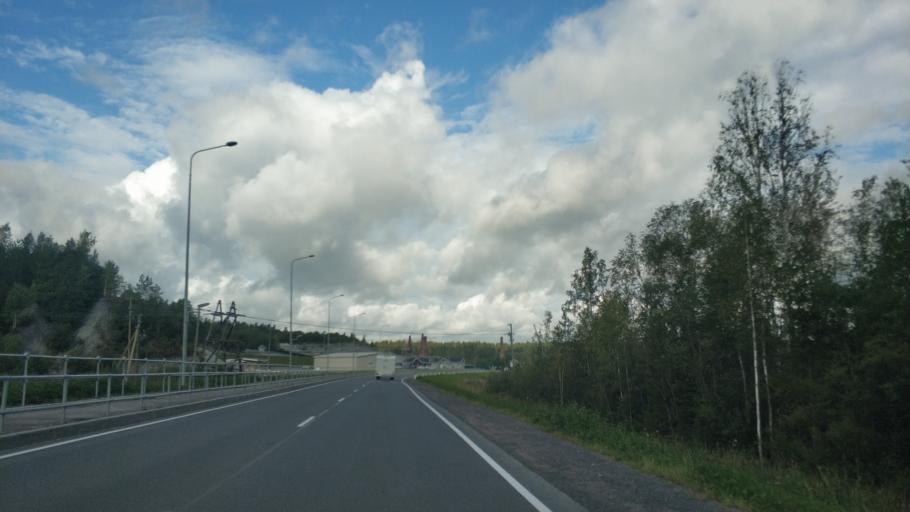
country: RU
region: Republic of Karelia
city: Ruskeala
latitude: 61.9476
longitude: 30.5907
